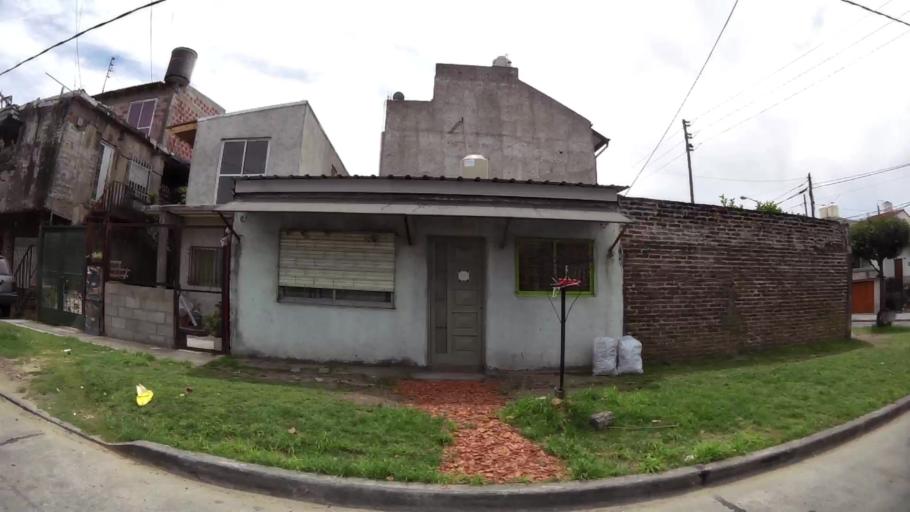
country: AR
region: Buenos Aires
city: San Justo
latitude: -34.6818
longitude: -58.5359
